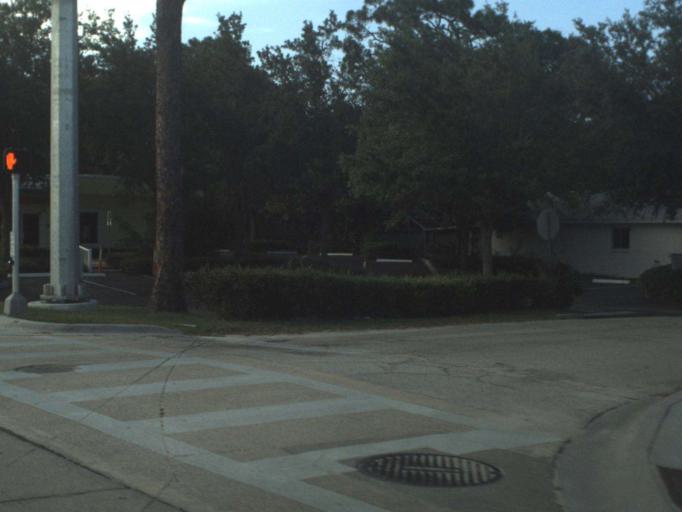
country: US
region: Florida
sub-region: Volusia County
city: Port Orange
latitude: 29.1451
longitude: -80.9883
